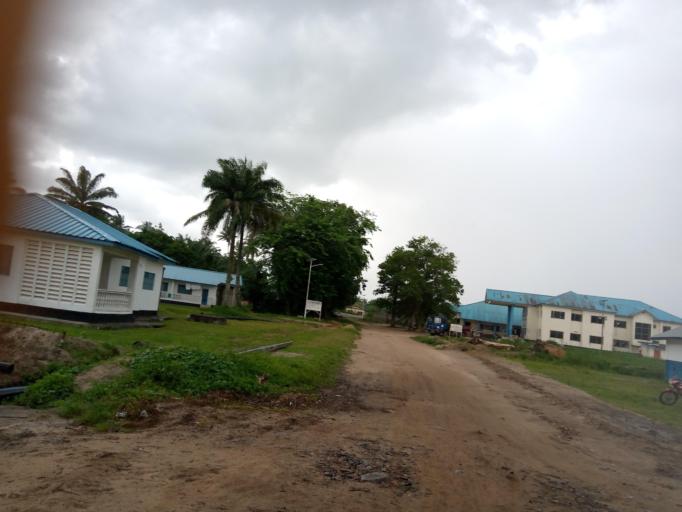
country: SL
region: Southern Province
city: Bonthe
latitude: 7.5291
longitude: -12.5070
